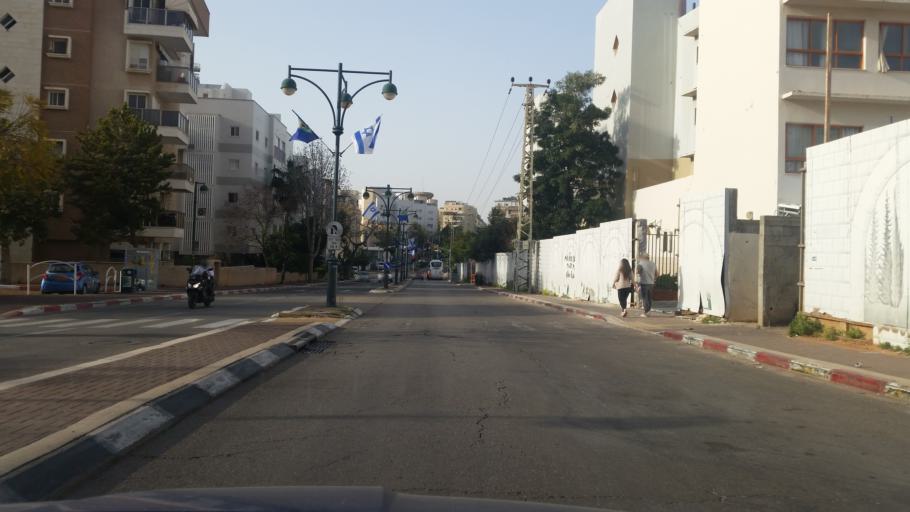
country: IL
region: Tel Aviv
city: Bene Beraq
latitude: 32.0735
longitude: 34.8331
